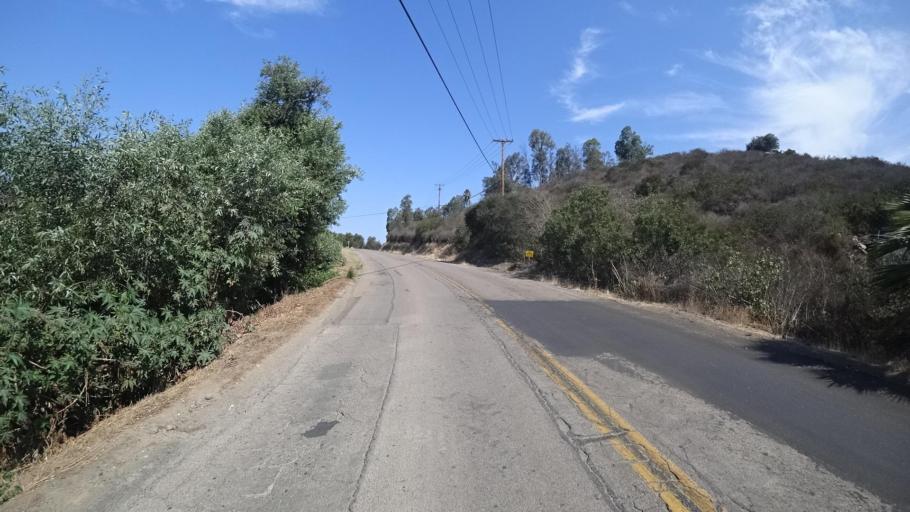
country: US
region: California
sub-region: San Diego County
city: Hidden Meadows
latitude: 33.2041
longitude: -117.1675
